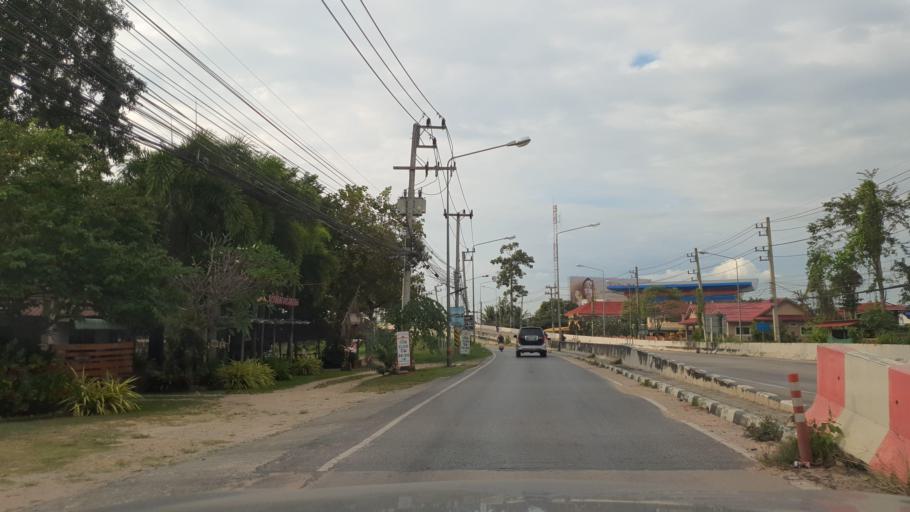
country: TH
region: Chon Buri
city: Phatthaya
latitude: 12.9470
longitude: 100.9367
